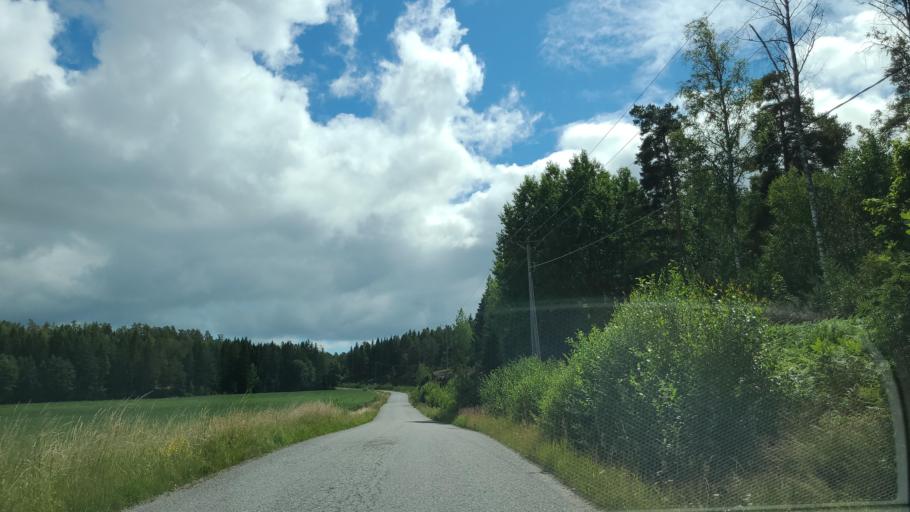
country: FI
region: Varsinais-Suomi
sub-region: Aboland-Turunmaa
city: Nagu
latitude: 60.1853
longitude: 22.0192
